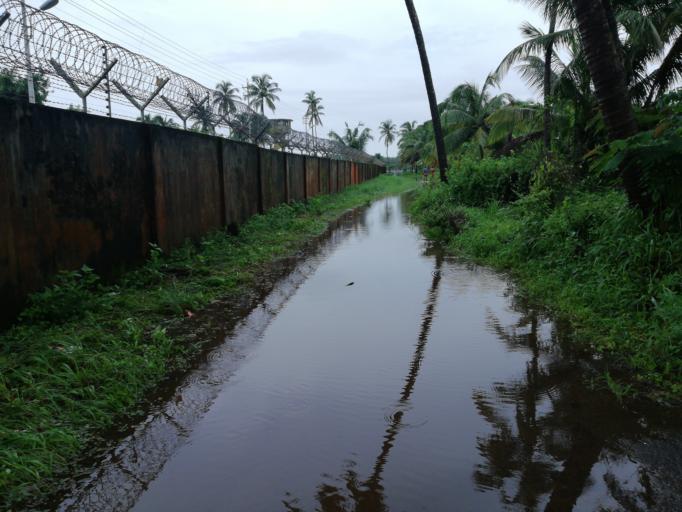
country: IN
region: Kerala
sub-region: Kannur
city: Payyannur
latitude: 12.0592
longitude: 75.1851
